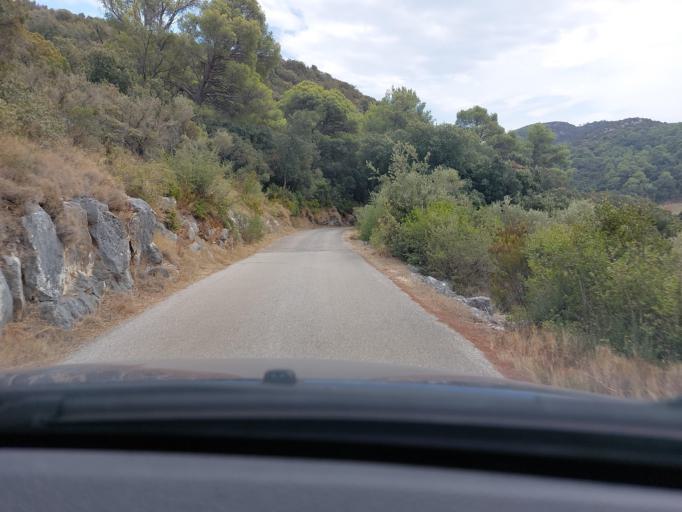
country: HR
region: Dubrovacko-Neretvanska
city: Smokvica
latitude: 42.7592
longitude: 16.9169
